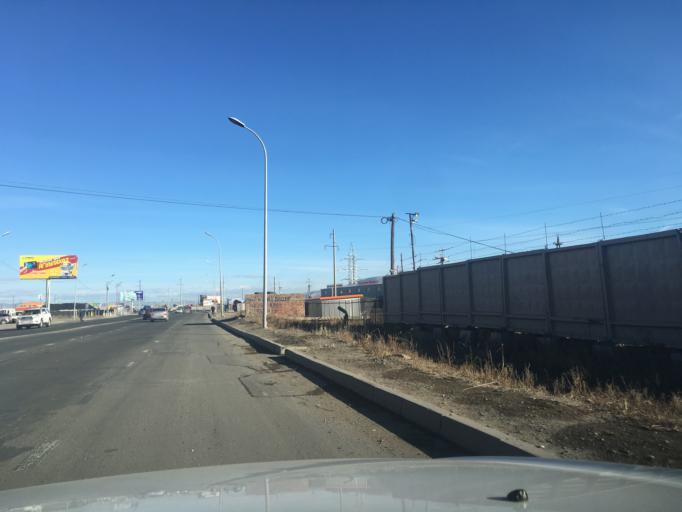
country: MN
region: Ulaanbaatar
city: Ulaanbaatar
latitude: 47.9023
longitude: 106.7365
